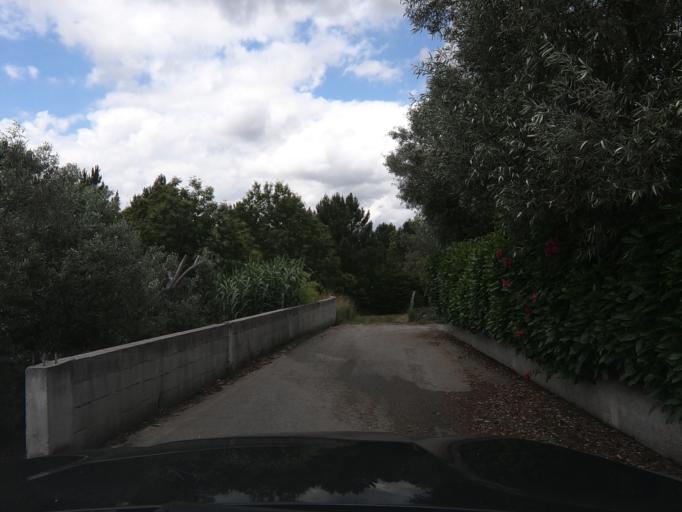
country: PT
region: Vila Real
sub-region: Sabrosa
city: Vilela
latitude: 41.2596
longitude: -7.6539
